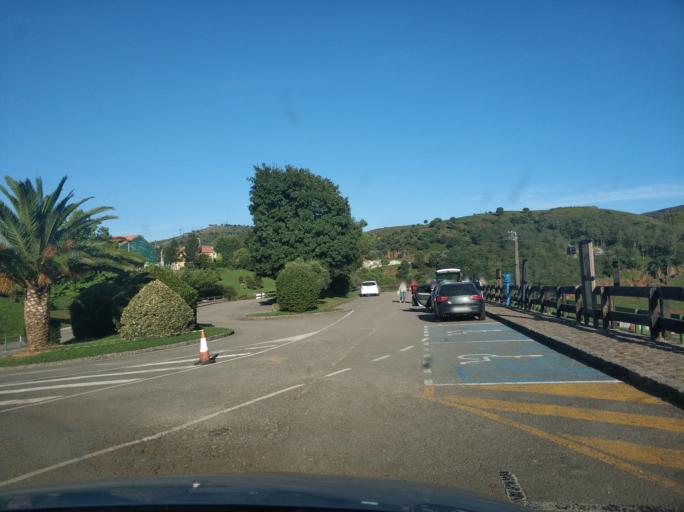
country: ES
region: Cantabria
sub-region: Provincia de Cantabria
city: Penagos
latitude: 43.3588
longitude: -3.8222
